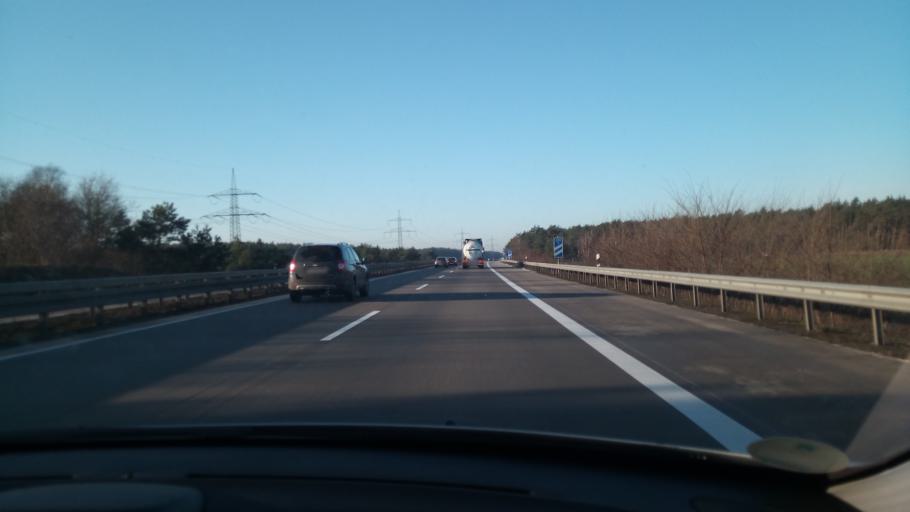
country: DE
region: Schleswig-Holstein
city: Besenthal
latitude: 53.5364
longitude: 10.7358
